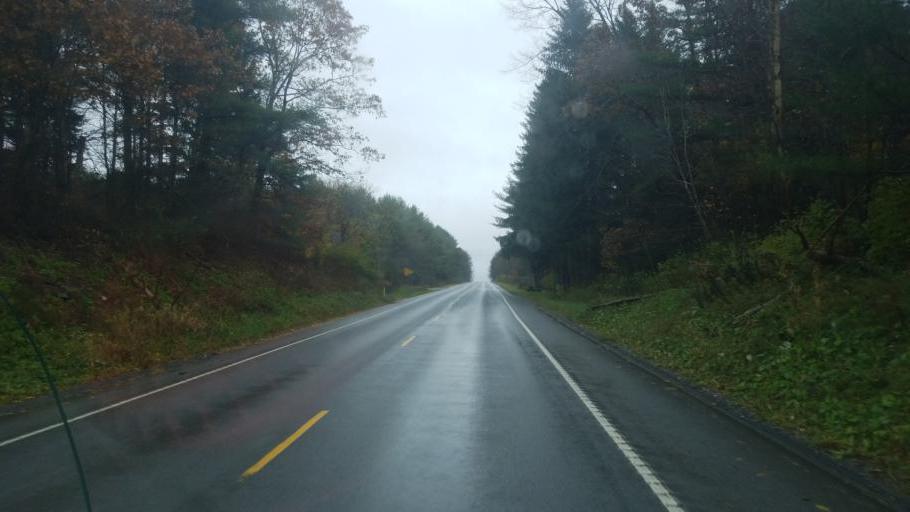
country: US
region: Pennsylvania
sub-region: Clearfield County
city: Shiloh
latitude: 41.1019
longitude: -78.1993
